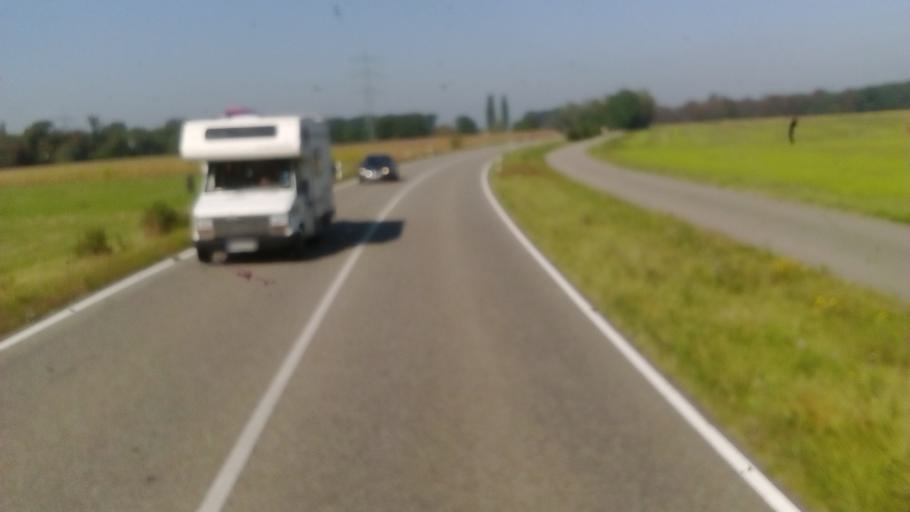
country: DE
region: Baden-Wuerttemberg
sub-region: Freiburg Region
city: Rheinau
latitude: 48.6531
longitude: 7.9665
